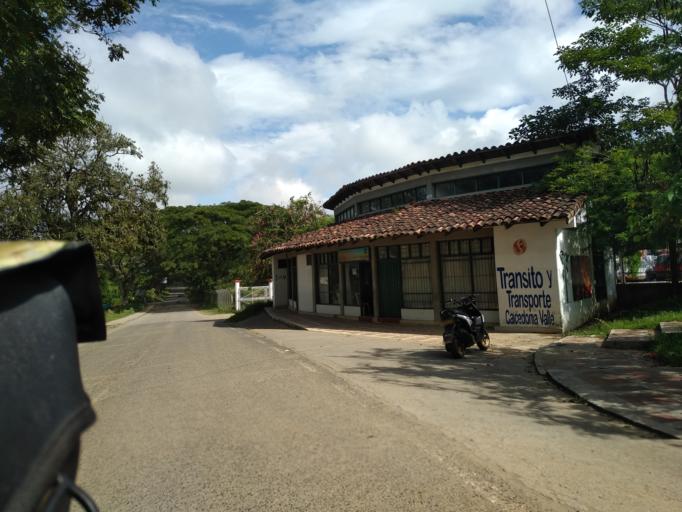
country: CO
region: Valle del Cauca
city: Caicedonia
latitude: 4.3403
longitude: -75.8299
